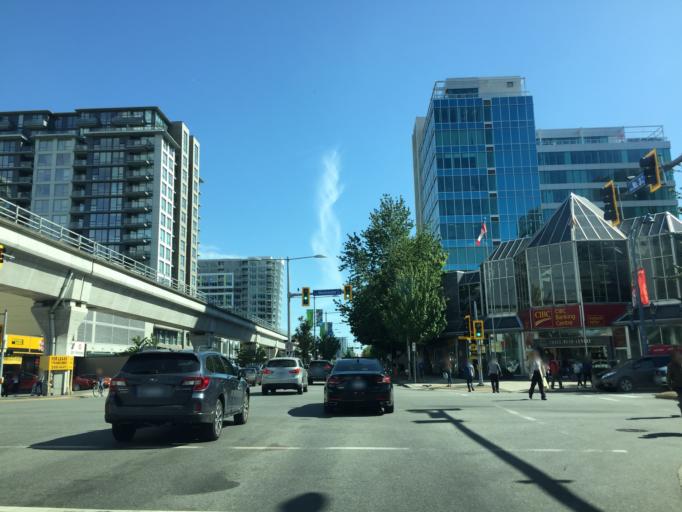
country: CA
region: British Columbia
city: Richmond
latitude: 49.1705
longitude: -123.1367
